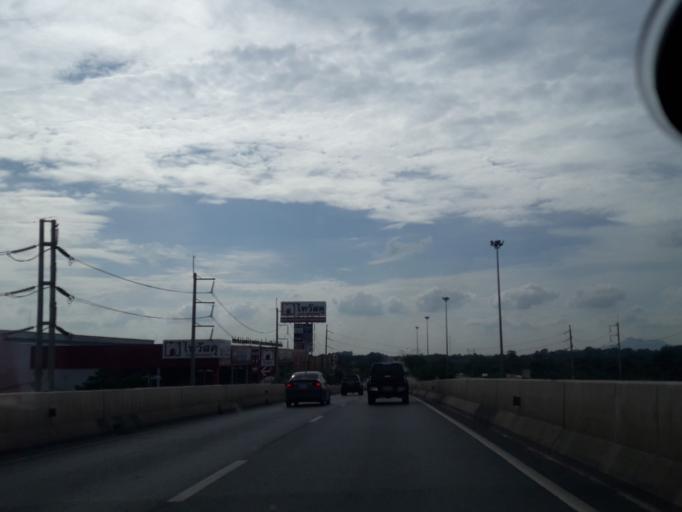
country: TH
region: Sara Buri
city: Saraburi
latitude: 14.5421
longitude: 100.9530
